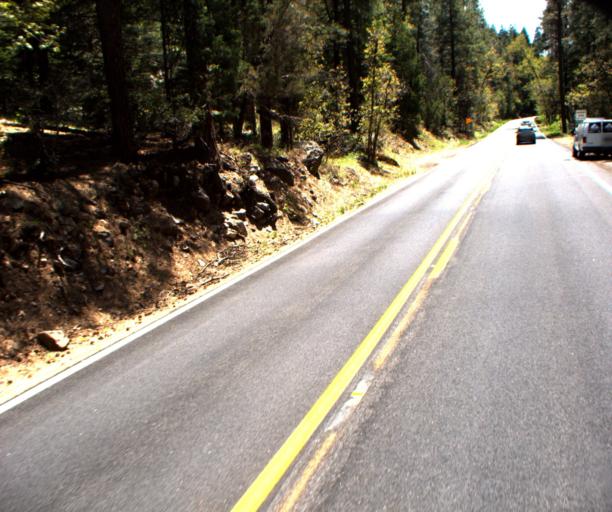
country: US
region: Arizona
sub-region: Coconino County
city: Kachina Village
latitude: 35.0177
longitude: -111.7373
